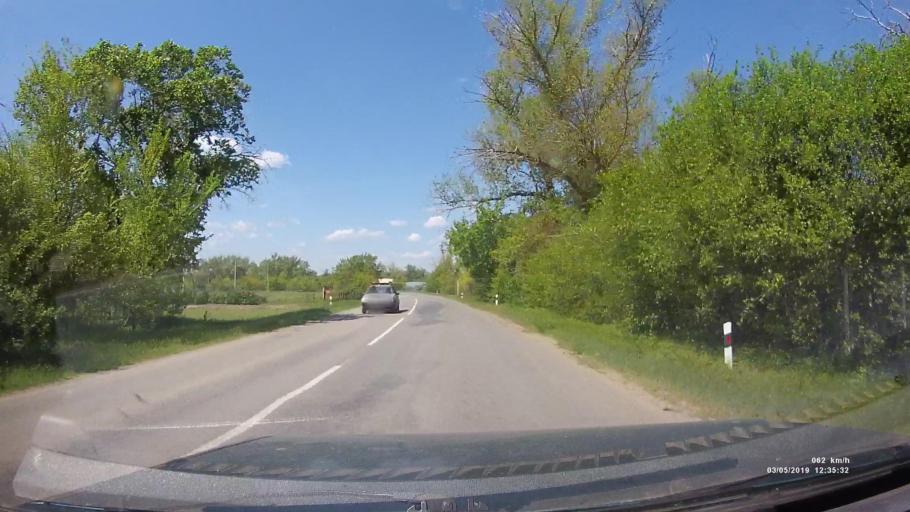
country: RU
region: Rostov
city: Semikarakorsk
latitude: 47.5275
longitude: 40.7602
